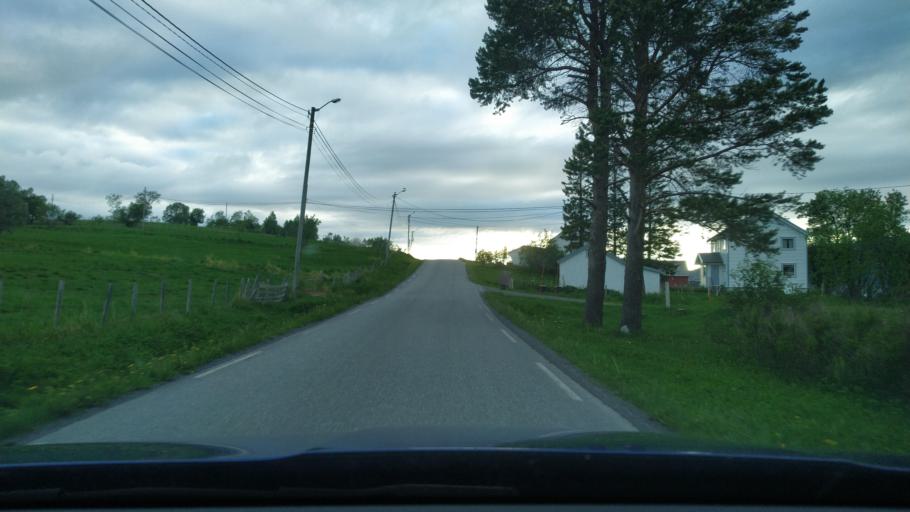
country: NO
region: Troms
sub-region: Tranoy
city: Vangsvika
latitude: 69.1264
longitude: 17.8525
